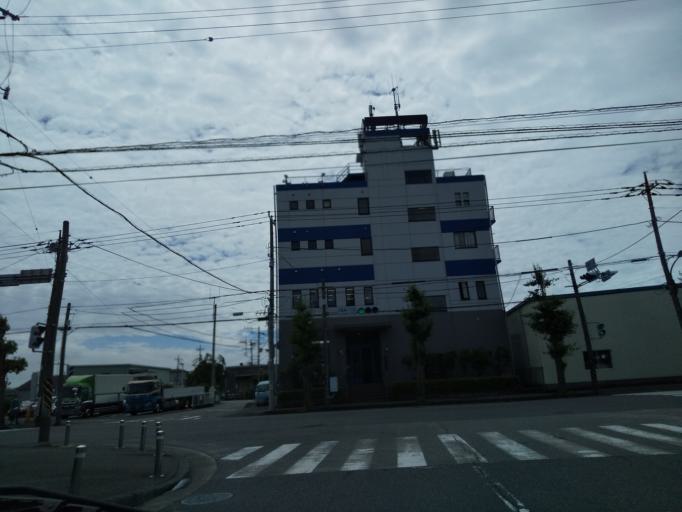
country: JP
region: Kanagawa
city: Zama
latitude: 35.5101
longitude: 139.3551
